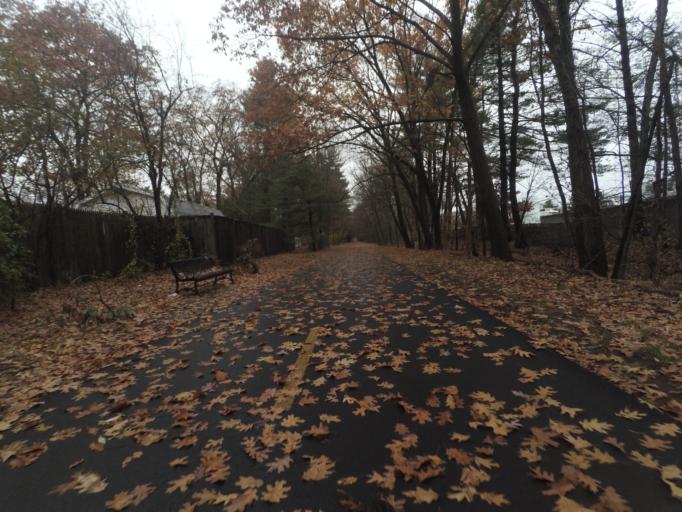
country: US
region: Massachusetts
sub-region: Middlesex County
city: Bedford
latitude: 42.4820
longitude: -71.2703
